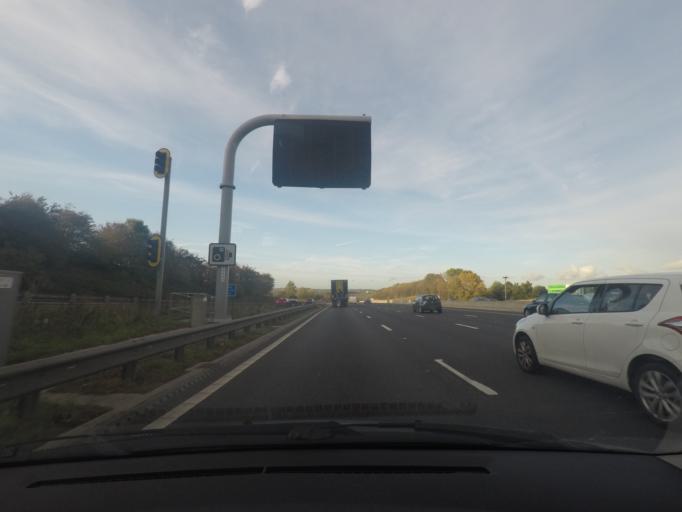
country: GB
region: England
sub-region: City and Borough of Wakefield
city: Ossett
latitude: 53.6858
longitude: -1.5558
